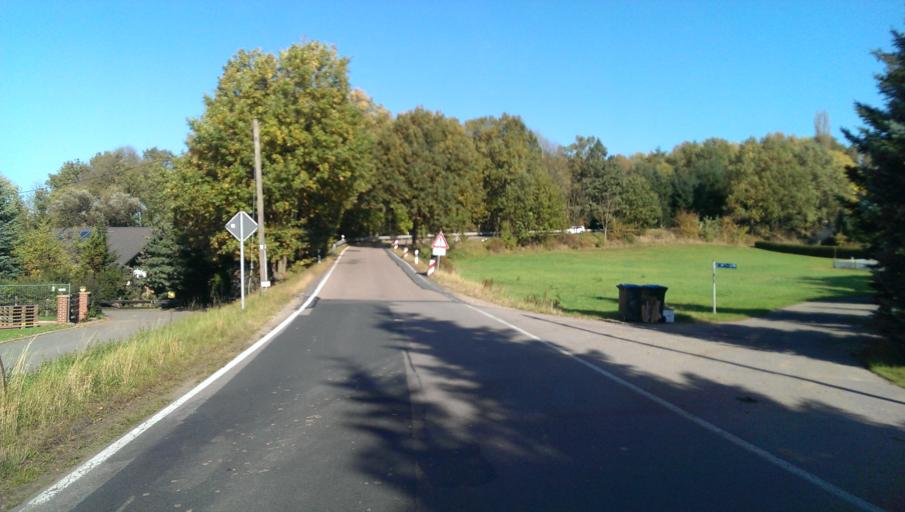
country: DE
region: Saxony
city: Dobeln
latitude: 51.1081
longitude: 13.0780
